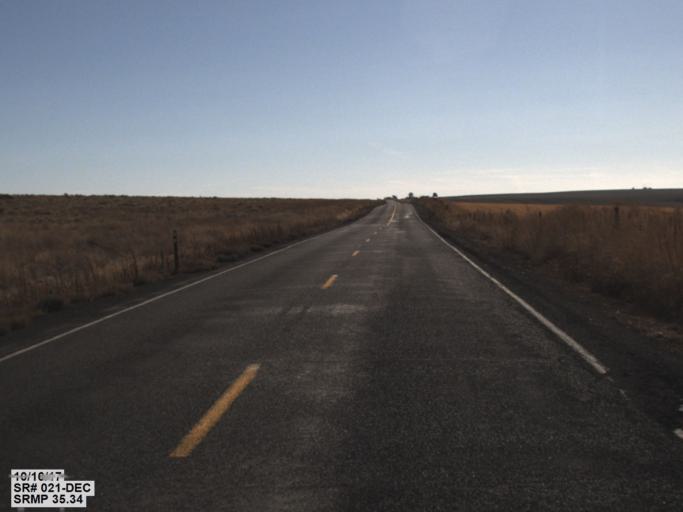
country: US
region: Washington
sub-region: Adams County
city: Ritzville
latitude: 47.0621
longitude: -118.6630
